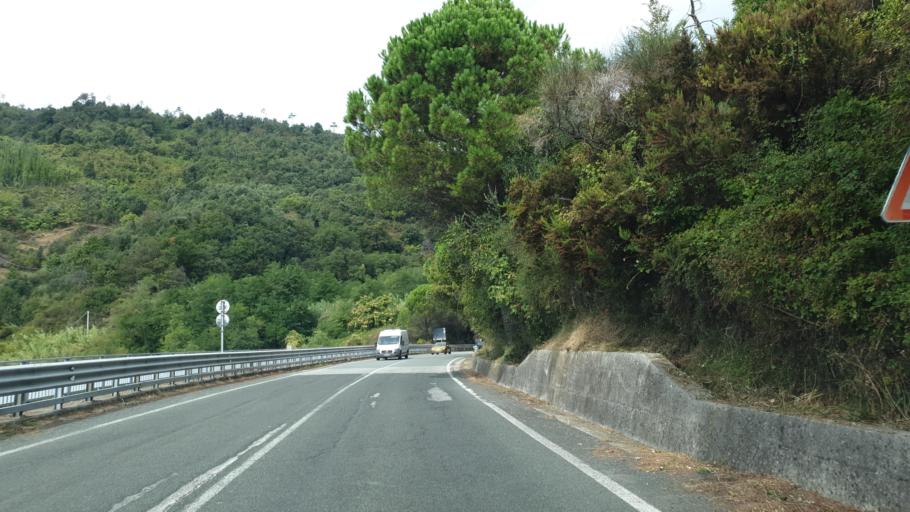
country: IT
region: Liguria
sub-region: Provincia di La Spezia
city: Levanto
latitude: 44.2003
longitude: 9.6235
